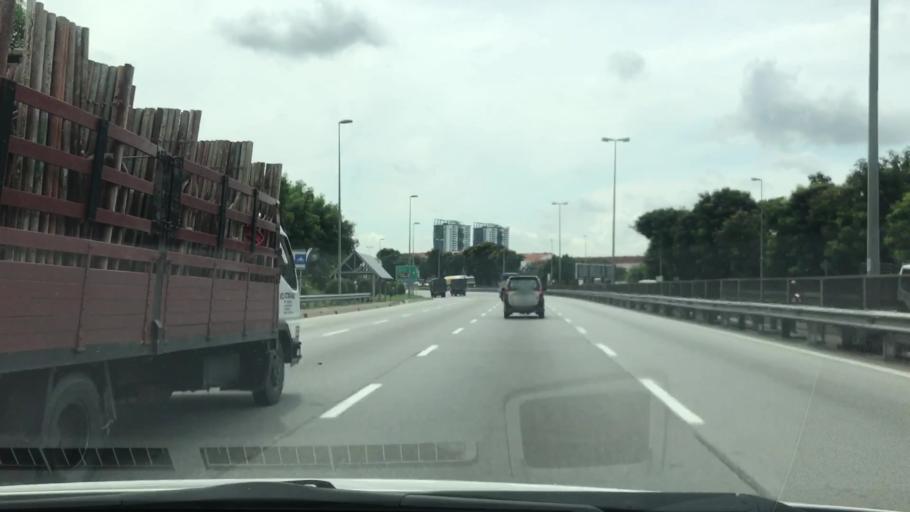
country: MY
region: Selangor
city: Subang Jaya
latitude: 2.9953
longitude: 101.6150
